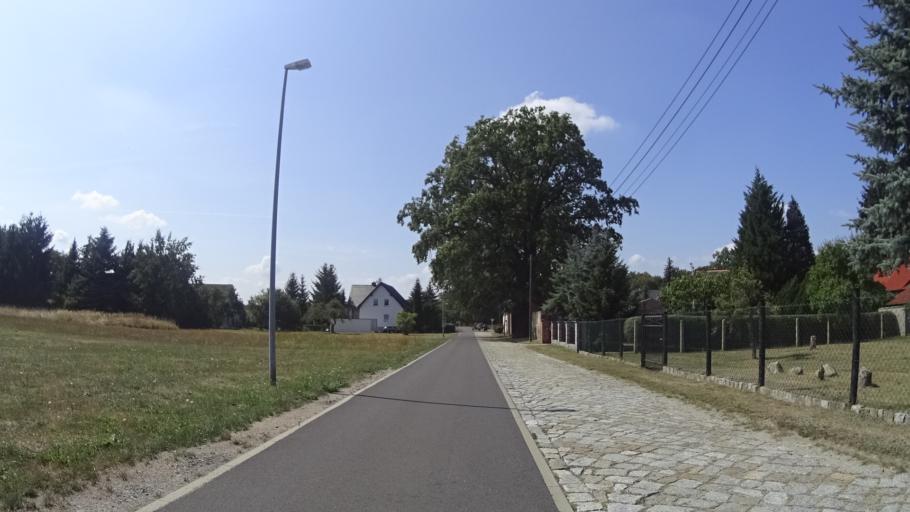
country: DE
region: Saxony
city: Gross Duben
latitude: 51.6069
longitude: 14.5082
